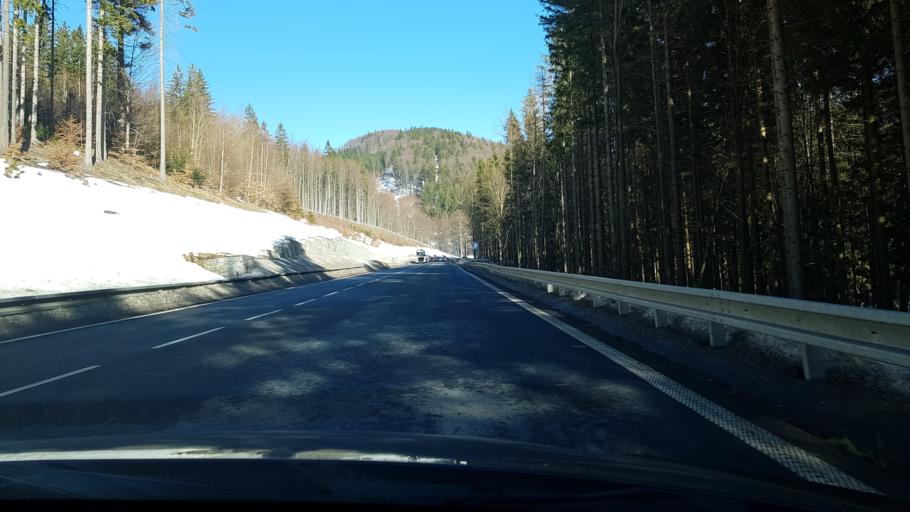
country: CZ
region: Olomoucky
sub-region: Okres Sumperk
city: Loucna nad Desnou
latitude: 50.1058
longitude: 17.1491
